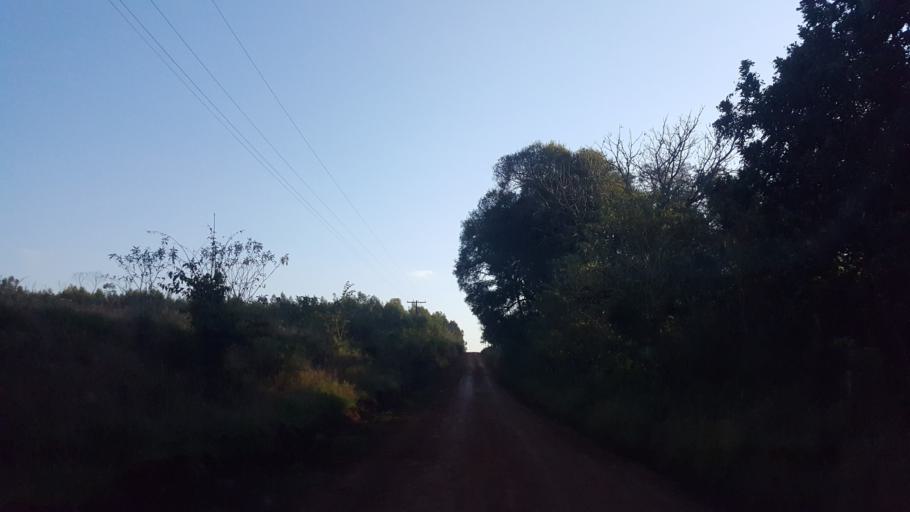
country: AR
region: Misiones
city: Capiovi
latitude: -26.9196
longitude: -55.0518
